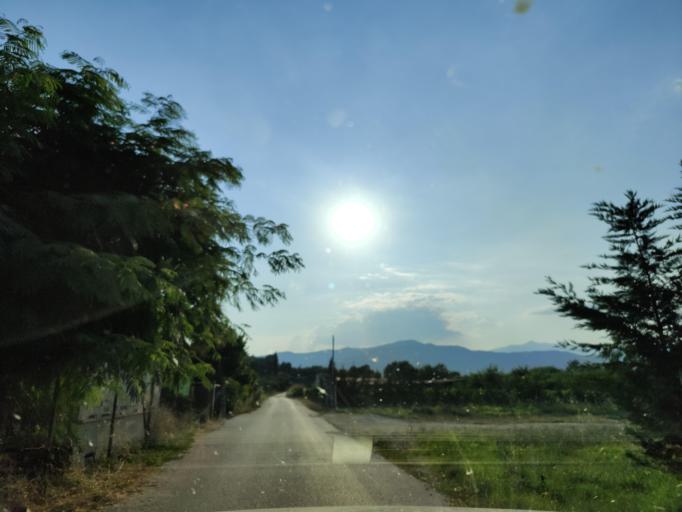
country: GR
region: East Macedonia and Thrace
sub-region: Nomos Kavalas
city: Nea Peramos
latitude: 40.8298
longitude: 24.2994
